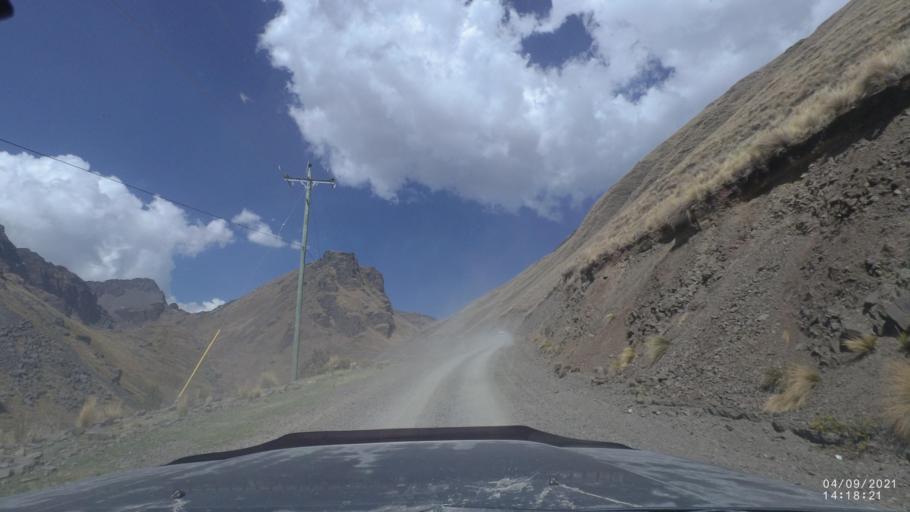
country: BO
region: Cochabamba
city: Sipe Sipe
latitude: -17.2306
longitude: -66.4292
